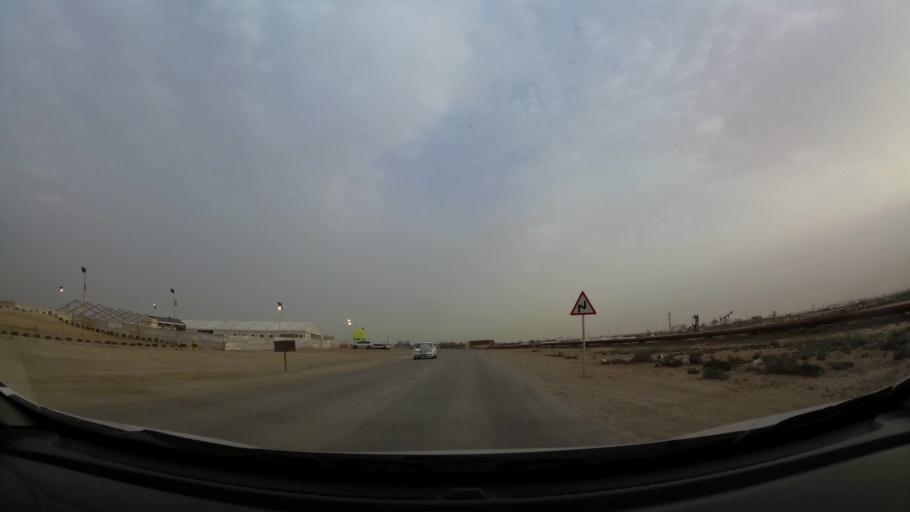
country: BH
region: Central Governorate
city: Dar Kulayb
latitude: 26.0085
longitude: 50.5810
